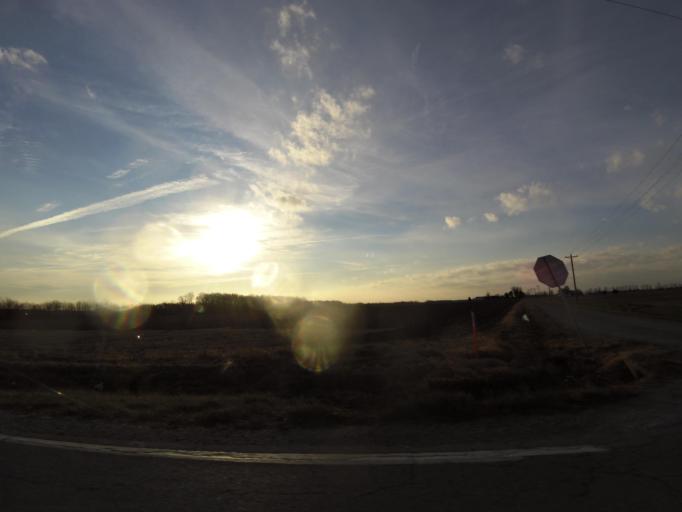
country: US
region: Illinois
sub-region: Fayette County
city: Vandalia
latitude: 38.9463
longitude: -89.1611
